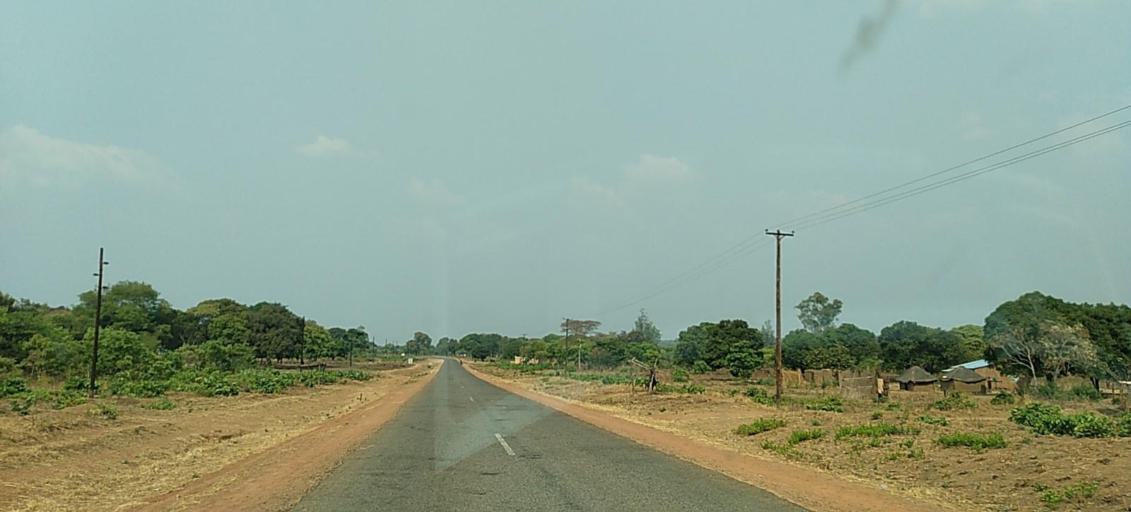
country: ZM
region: North-Western
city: Kabompo
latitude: -13.5354
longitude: 24.2781
